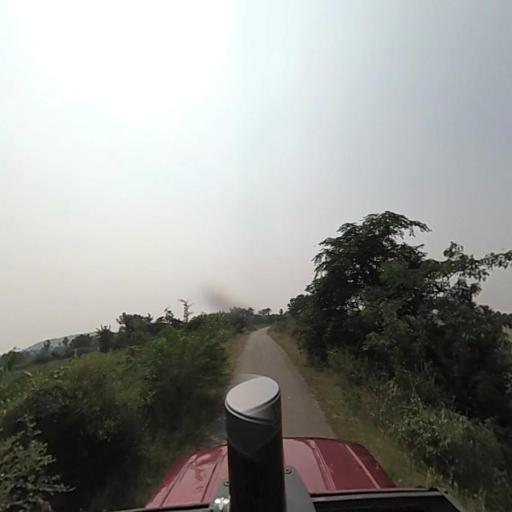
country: IN
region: Telangana
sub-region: Nalgonda
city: Nalgonda
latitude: 17.1985
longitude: 79.1408
